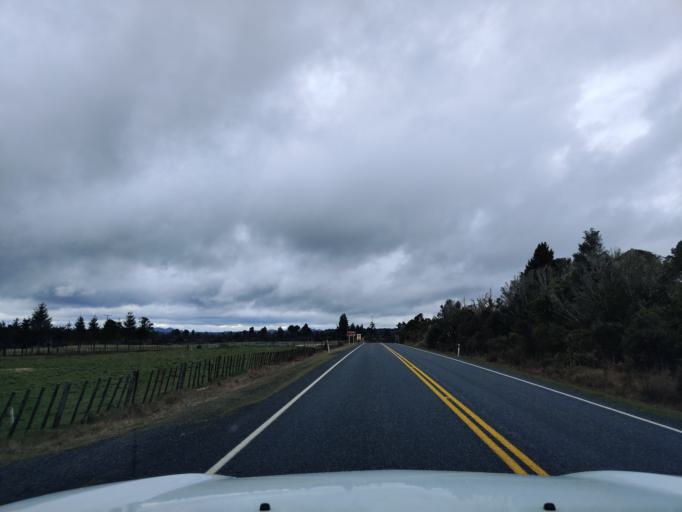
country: NZ
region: Manawatu-Wanganui
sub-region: Ruapehu District
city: Waiouru
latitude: -39.2835
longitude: 175.3864
